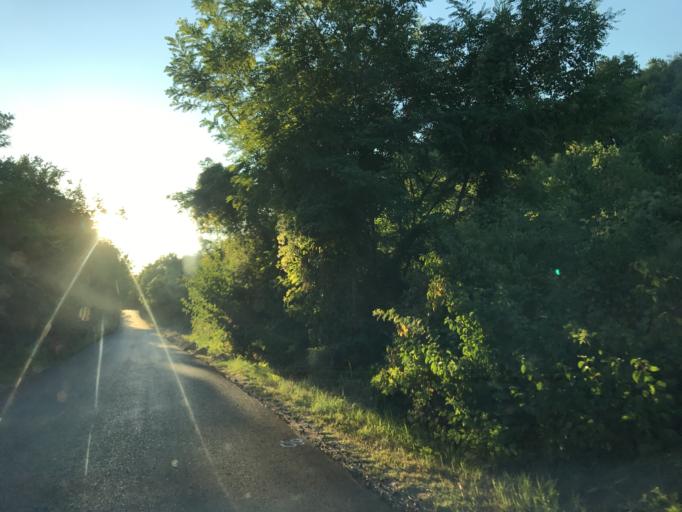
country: BG
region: Vidin
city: Bregovo
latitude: 44.1200
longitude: 22.5889
